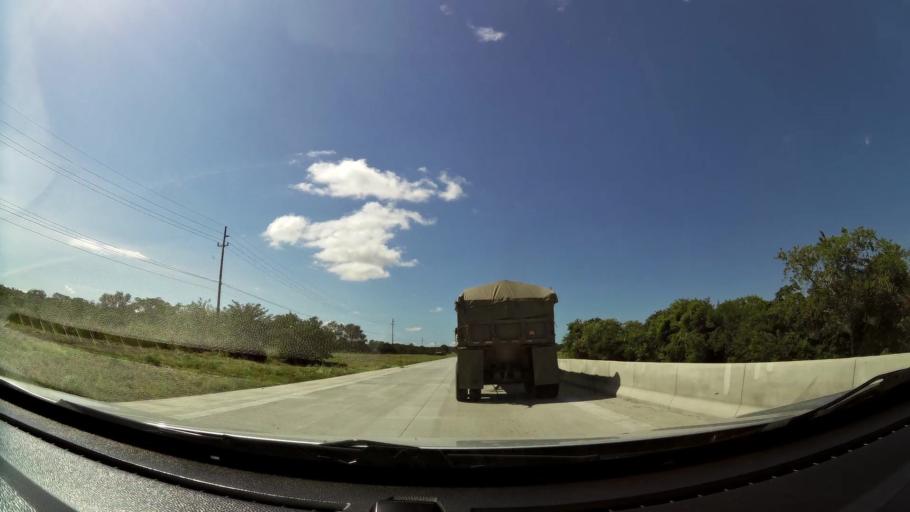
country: CR
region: Guanacaste
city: Bagaces
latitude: 10.5402
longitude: -85.3111
